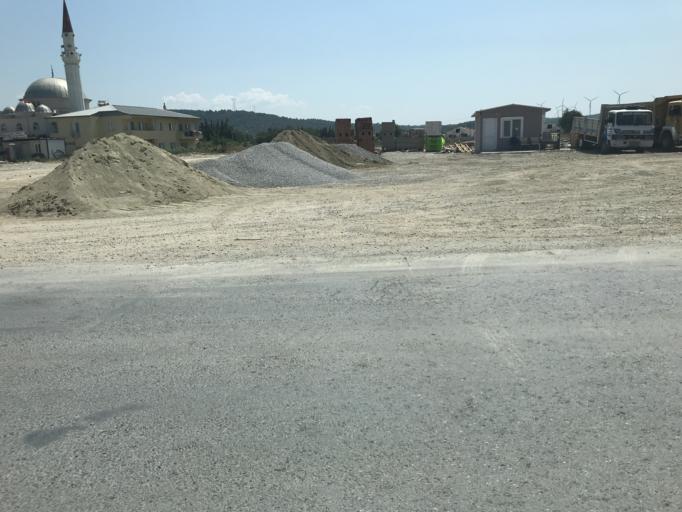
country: TR
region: Izmir
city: Urla
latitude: 38.2782
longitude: 26.7406
